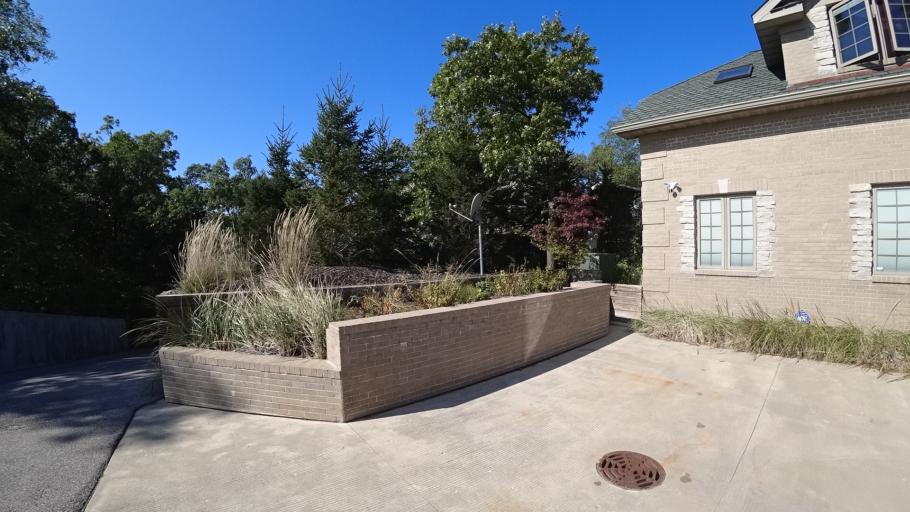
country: US
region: Indiana
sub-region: LaPorte County
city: Long Beach
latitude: 41.7336
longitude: -86.8797
